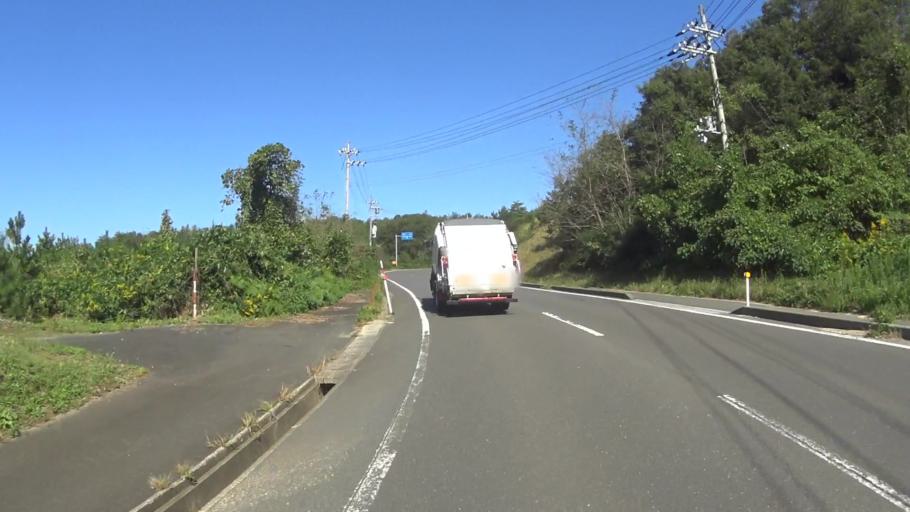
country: JP
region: Kyoto
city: Miyazu
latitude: 35.6943
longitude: 135.0509
